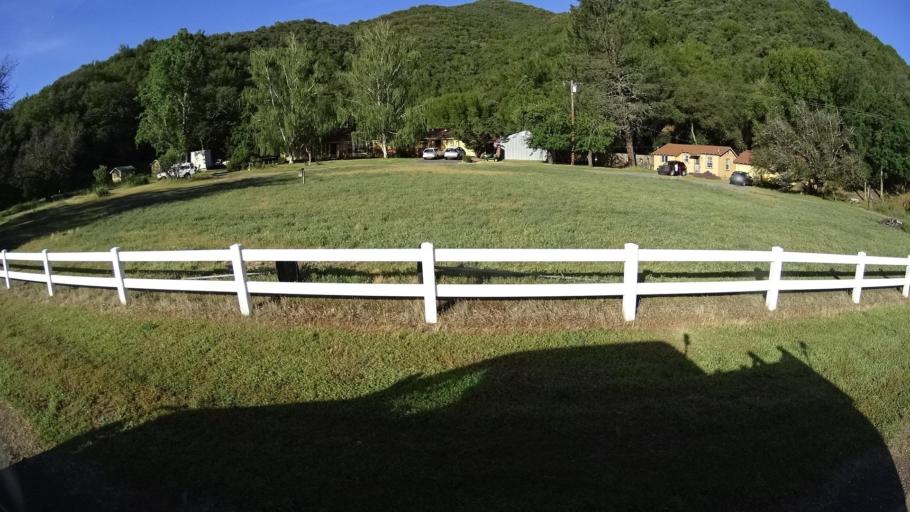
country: US
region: California
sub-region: Lake County
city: Upper Lake
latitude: 39.1403
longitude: -123.0016
